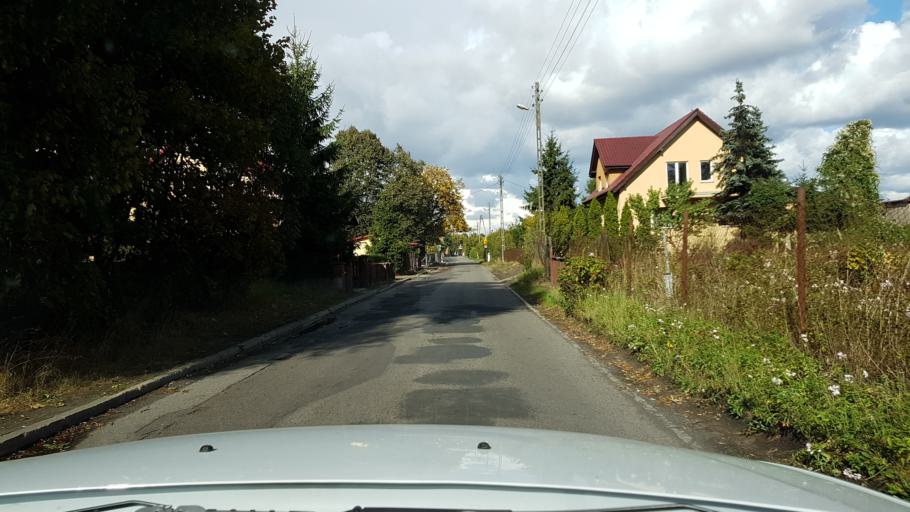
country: PL
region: West Pomeranian Voivodeship
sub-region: Powiat gryfinski
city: Gryfino
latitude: 53.2853
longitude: 14.4974
